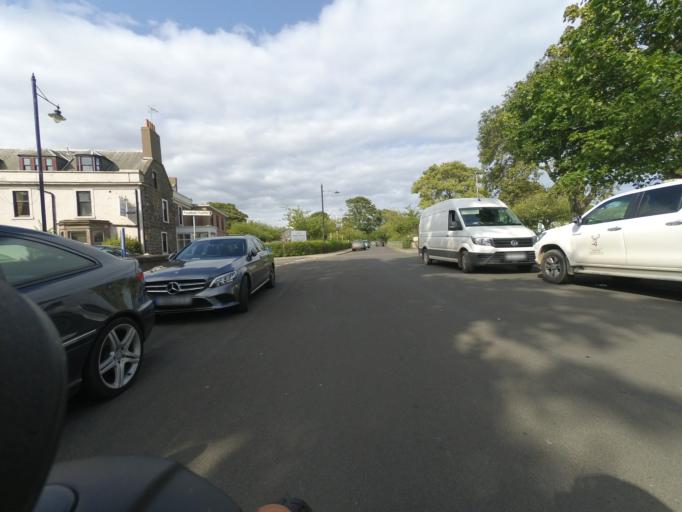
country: GB
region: Scotland
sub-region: Angus
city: Montrose
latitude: 56.7127
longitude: -2.4635
